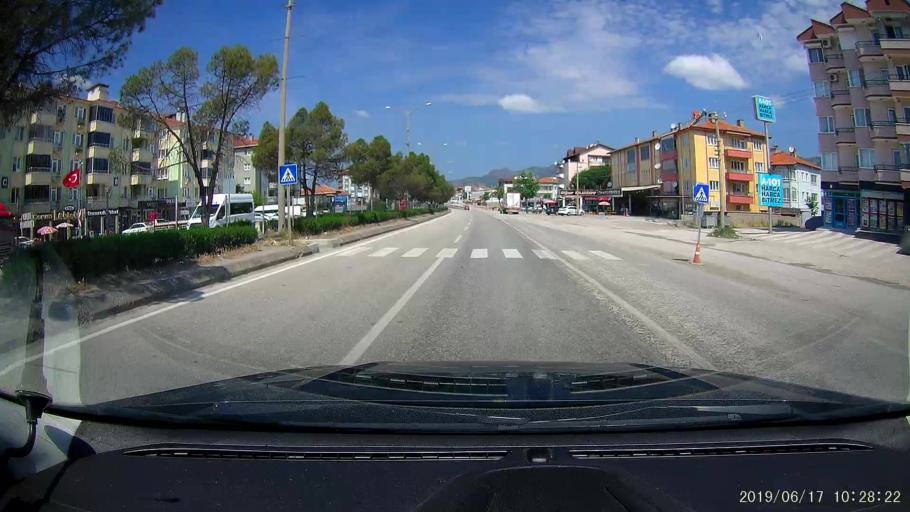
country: TR
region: Corum
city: Osmancik
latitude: 40.9778
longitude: 34.8089
